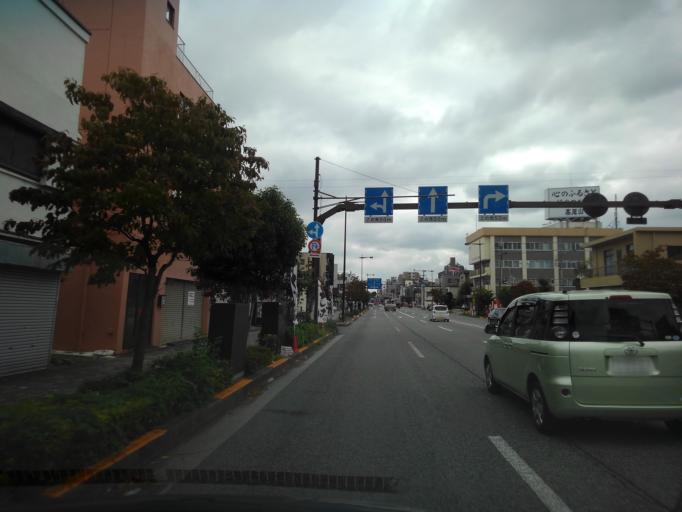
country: JP
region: Tokyo
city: Hachioji
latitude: 35.6651
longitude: 139.3300
